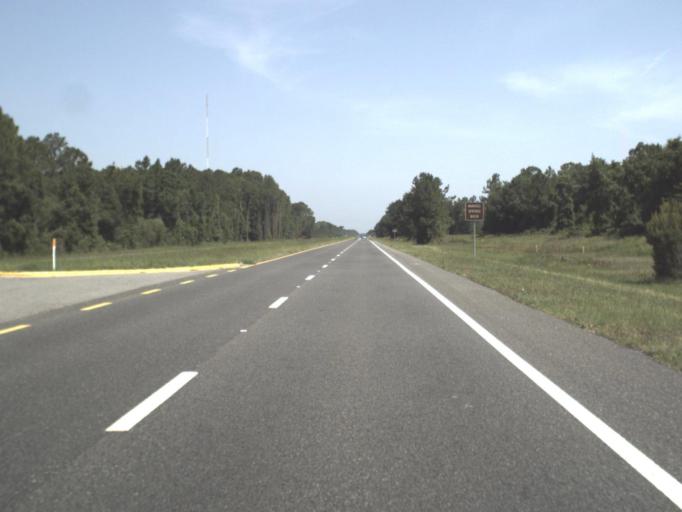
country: US
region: Florida
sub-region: Levy County
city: Chiefland
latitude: 29.4030
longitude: -82.8147
